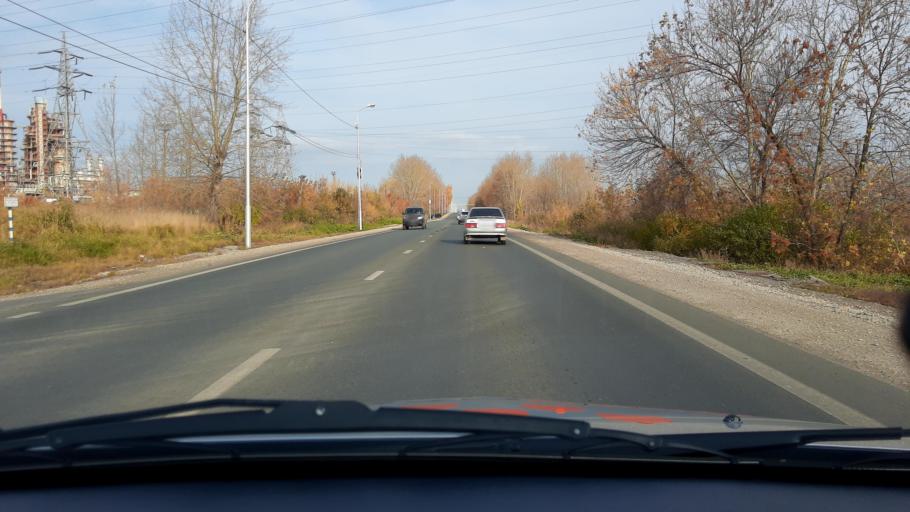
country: RU
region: Bashkortostan
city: Ufa
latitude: 54.8507
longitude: 56.1176
